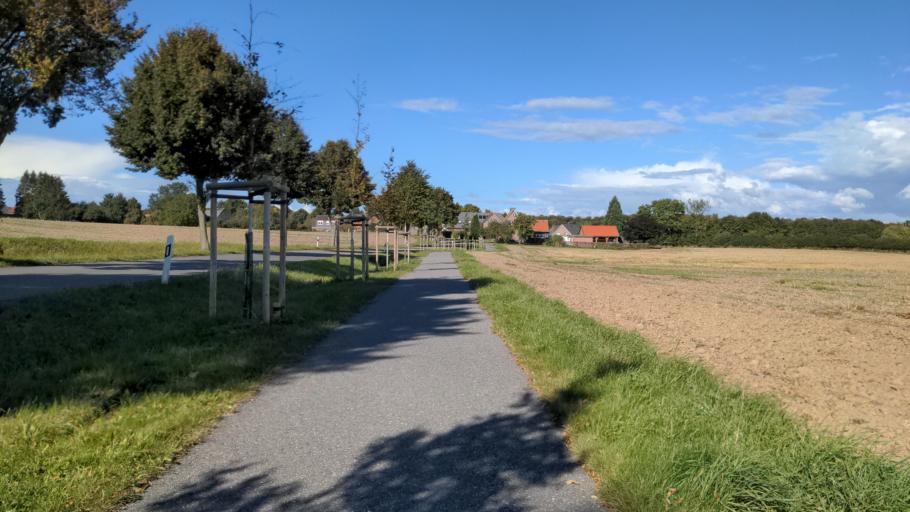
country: DE
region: Schleswig-Holstein
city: Gromitz
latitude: 54.1698
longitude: 10.9388
